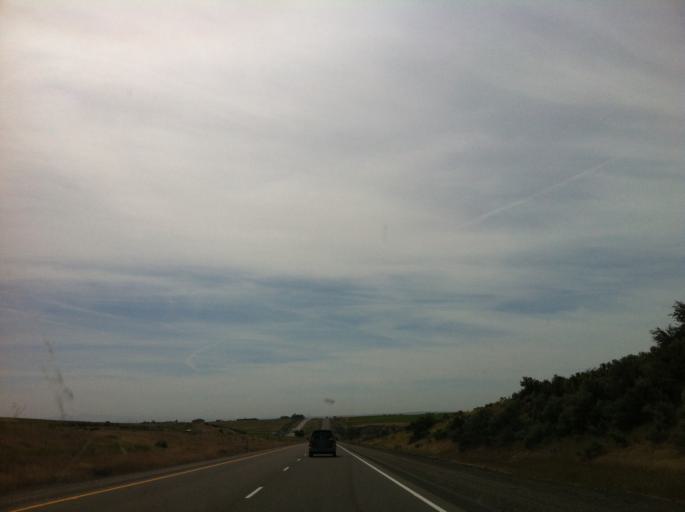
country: US
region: Oregon
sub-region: Malheur County
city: Ontario
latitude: 44.1028
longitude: -117.0441
